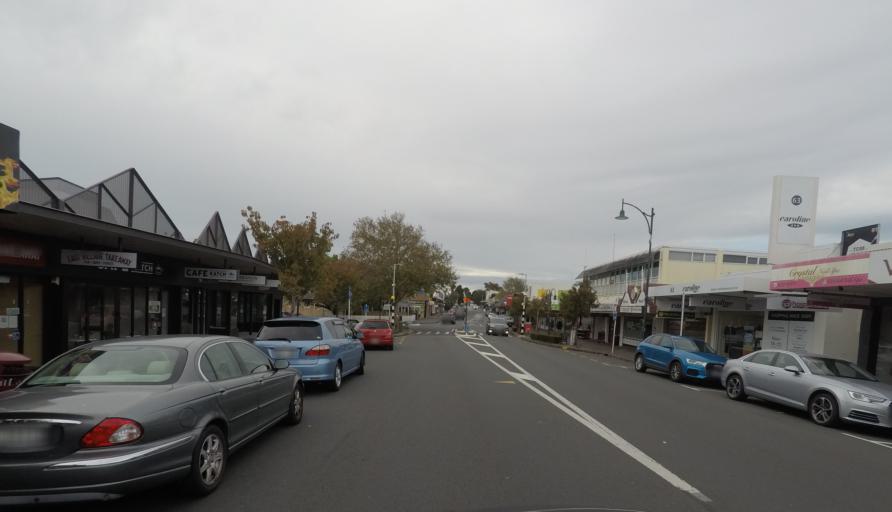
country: NZ
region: Auckland
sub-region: Auckland
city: Pakuranga
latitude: -36.8937
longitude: 174.9312
